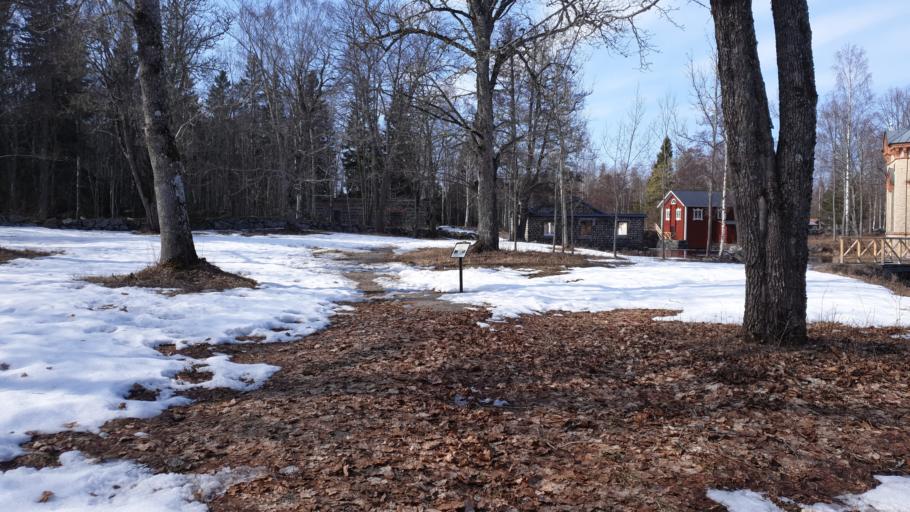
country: SE
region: Gaevleborg
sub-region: Gavle Kommun
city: Norrsundet
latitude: 61.0459
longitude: 17.1411
